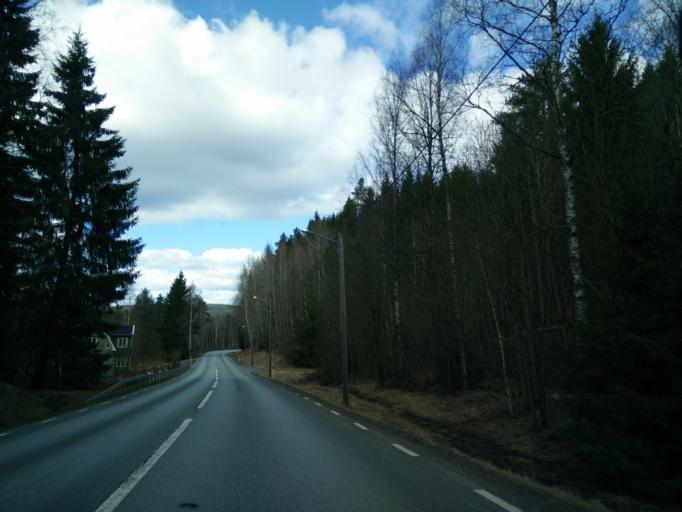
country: SE
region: Vaermland
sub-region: Munkfors Kommun
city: Munkfors
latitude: 59.8901
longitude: 13.5640
